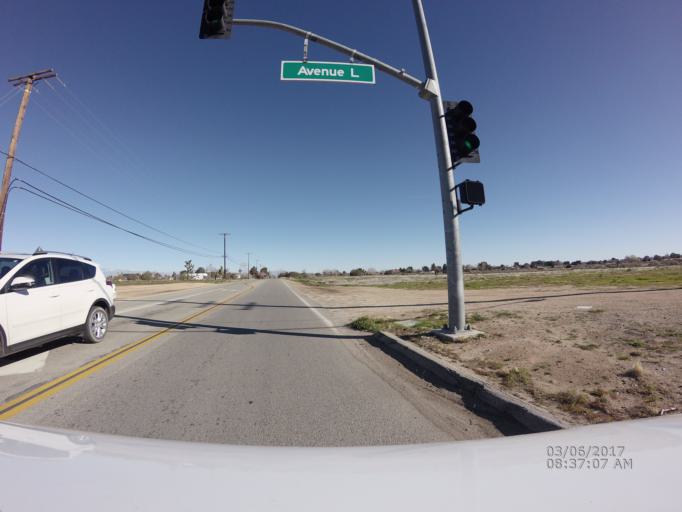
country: US
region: California
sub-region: Los Angeles County
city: Quartz Hill
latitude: 34.6604
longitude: -118.2100
